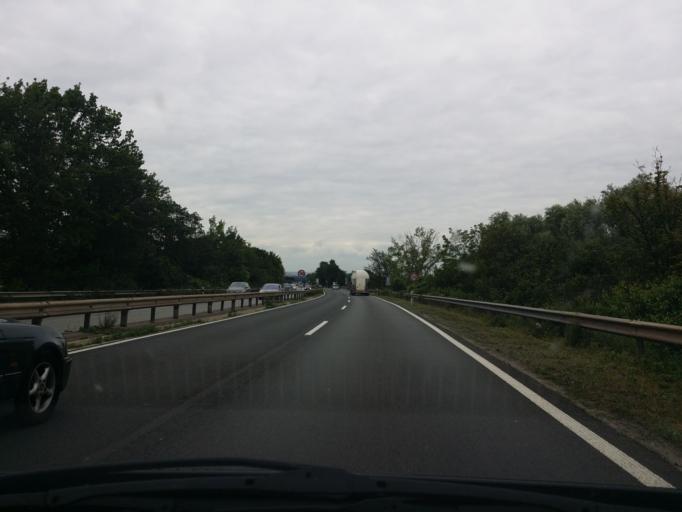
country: DE
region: Rheinland-Pfalz
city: Klein-Winternheim
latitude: 49.9825
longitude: 8.2068
